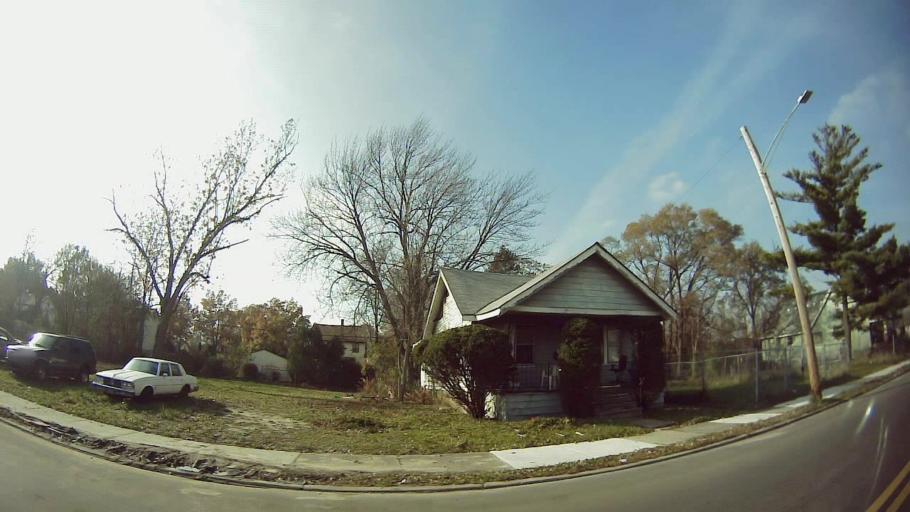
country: US
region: Michigan
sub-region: Wayne County
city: Highland Park
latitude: 42.4083
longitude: -83.1355
